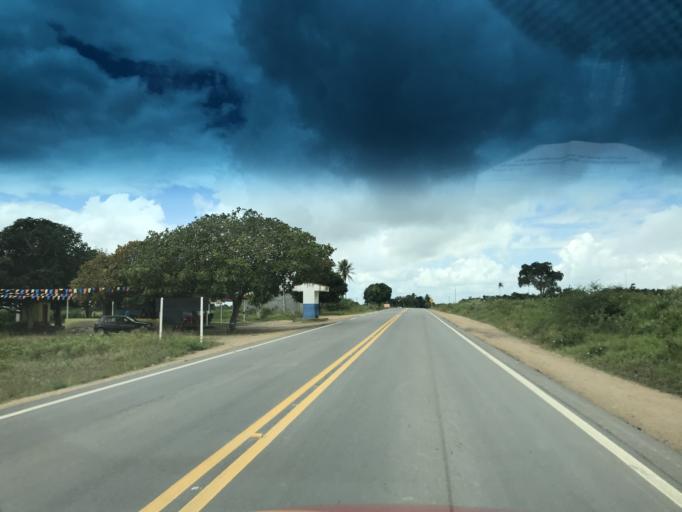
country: BR
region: Bahia
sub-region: Conceicao Do Almeida
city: Conceicao do Almeida
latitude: -12.6941
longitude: -39.2444
